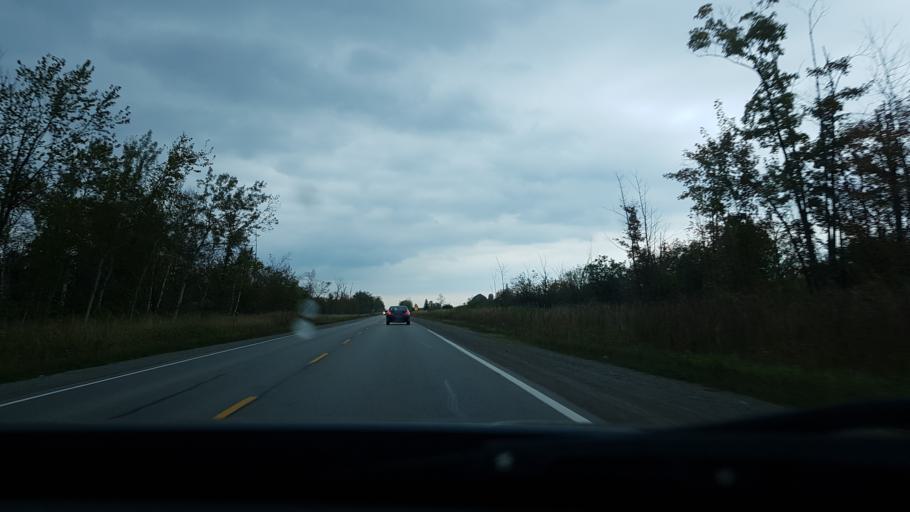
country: CA
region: Ontario
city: Omemee
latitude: 44.3694
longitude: -78.6753
